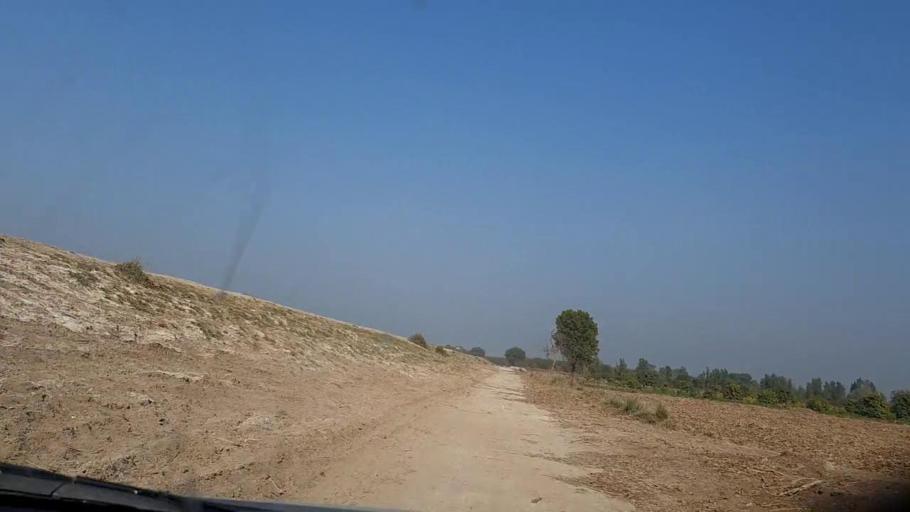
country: PK
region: Sindh
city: Moro
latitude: 26.8079
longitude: 67.9520
